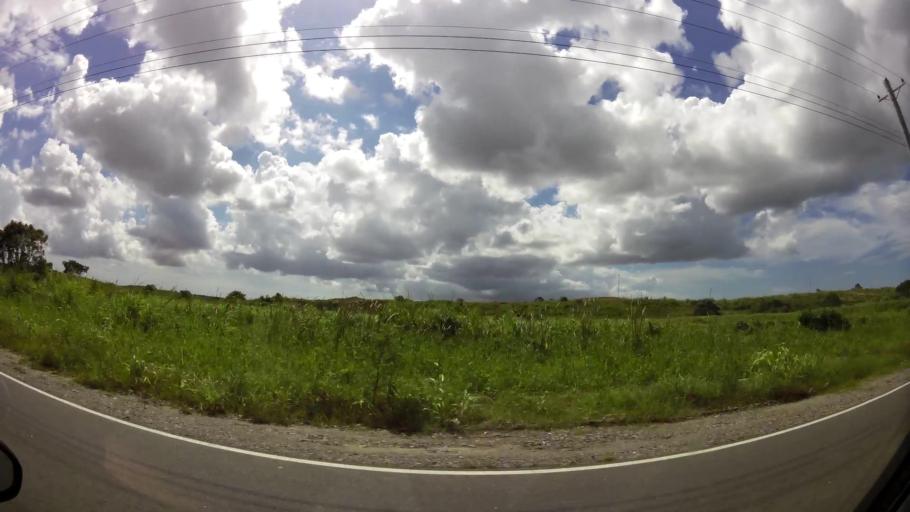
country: TT
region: Penal/Debe
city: Debe
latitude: 10.2315
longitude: -61.4933
